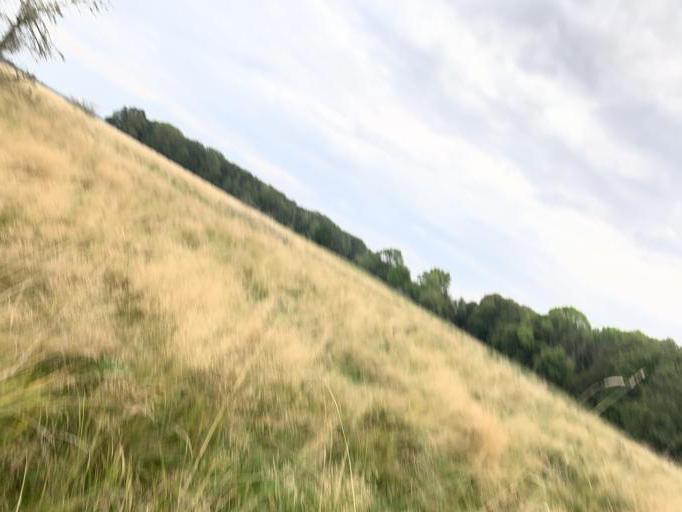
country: SE
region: Vaestmanland
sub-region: Hallstahammars Kommun
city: Kolback
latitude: 59.4723
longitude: 16.2172
